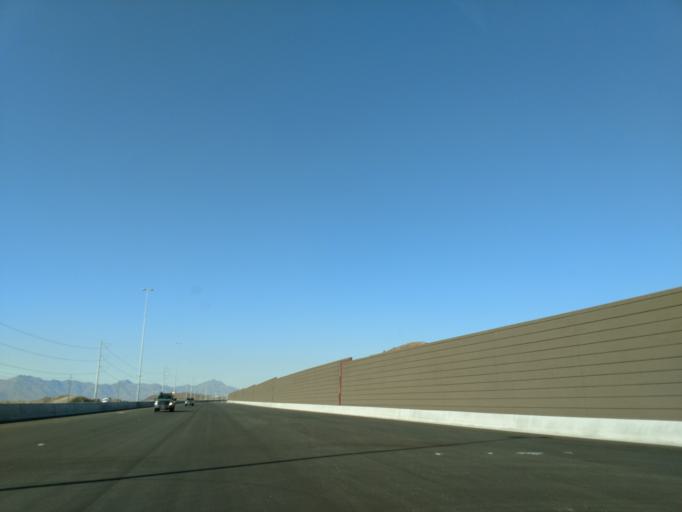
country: US
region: Arizona
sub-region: Maricopa County
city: Guadalupe
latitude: 33.2920
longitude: -112.0362
